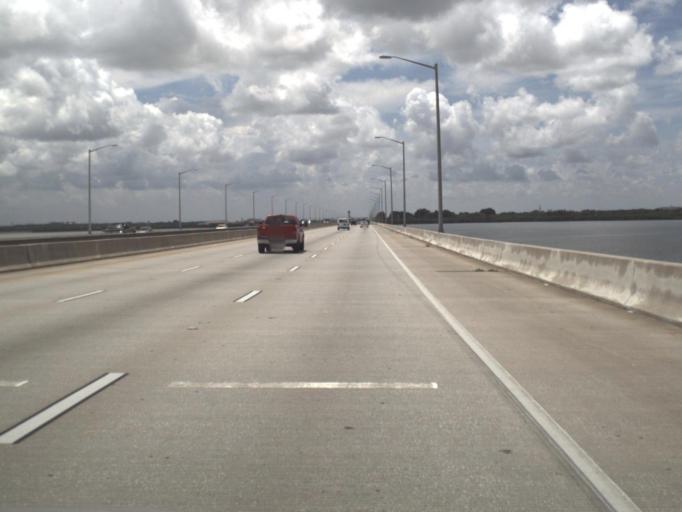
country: US
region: Florida
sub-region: Pinellas County
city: South Highpoint
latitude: 27.9411
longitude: -82.7039
